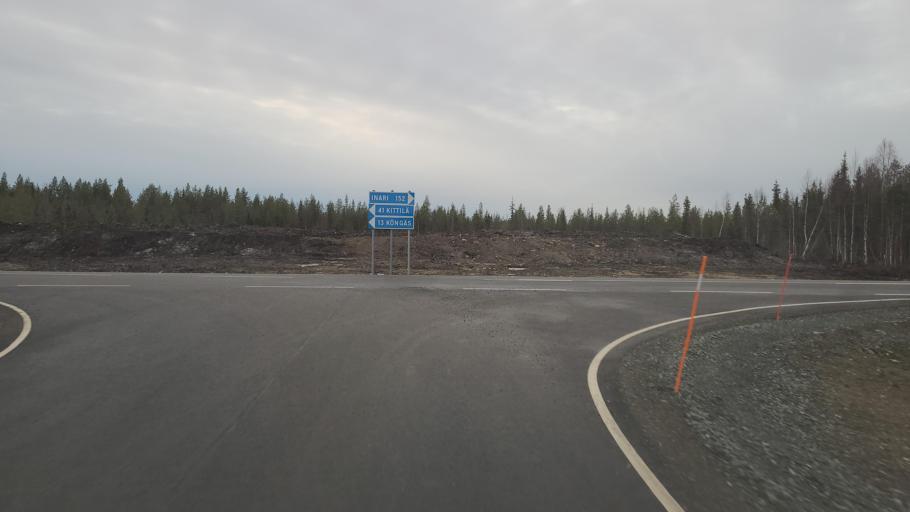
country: FI
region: Lapland
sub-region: Tunturi-Lappi
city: Kittilae
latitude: 67.9040
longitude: 25.0793
